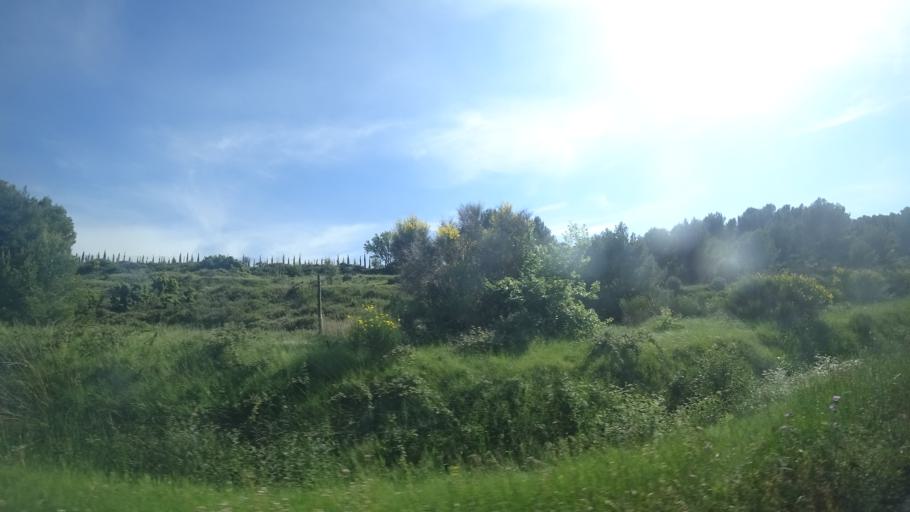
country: FR
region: Languedoc-Roussillon
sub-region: Departement de l'Aude
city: Ginestas
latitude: 43.2847
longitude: 2.8357
